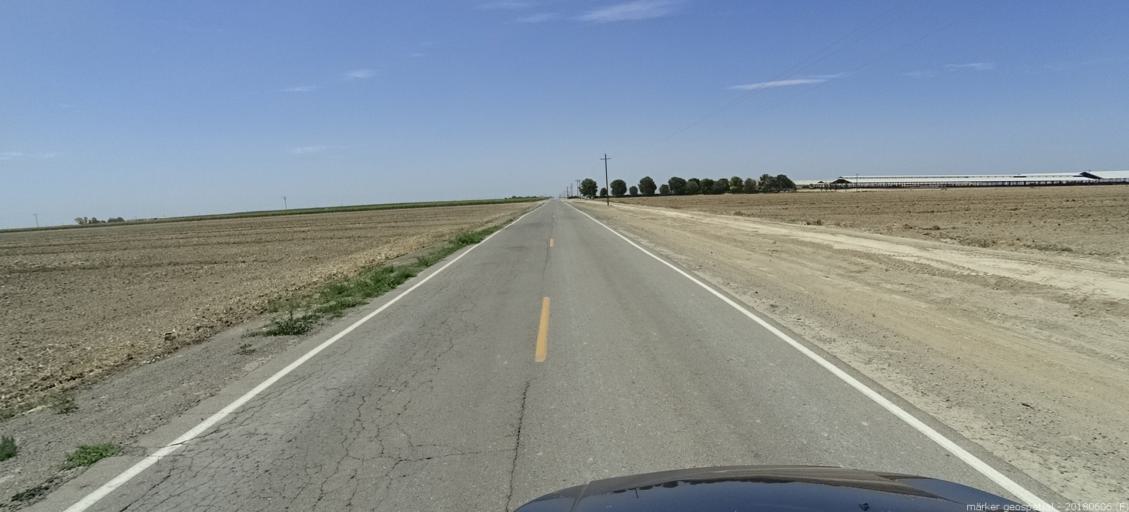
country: US
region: California
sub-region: Fresno County
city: Firebaugh
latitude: 36.9406
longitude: -120.3824
